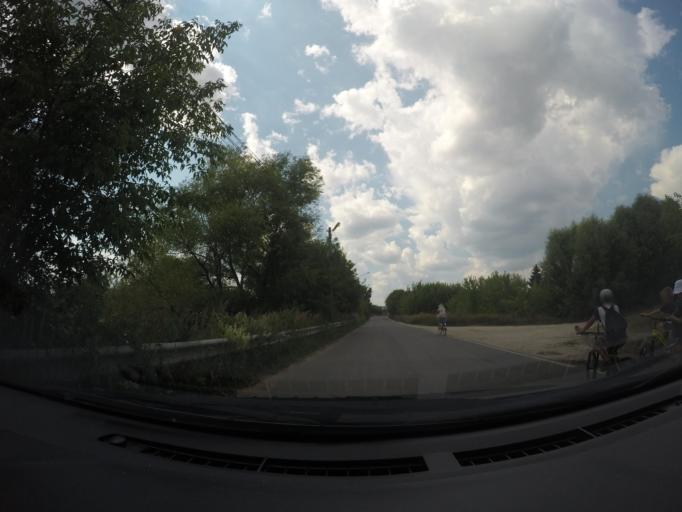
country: RU
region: Moskovskaya
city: Rechitsy
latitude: 55.5831
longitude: 38.5132
